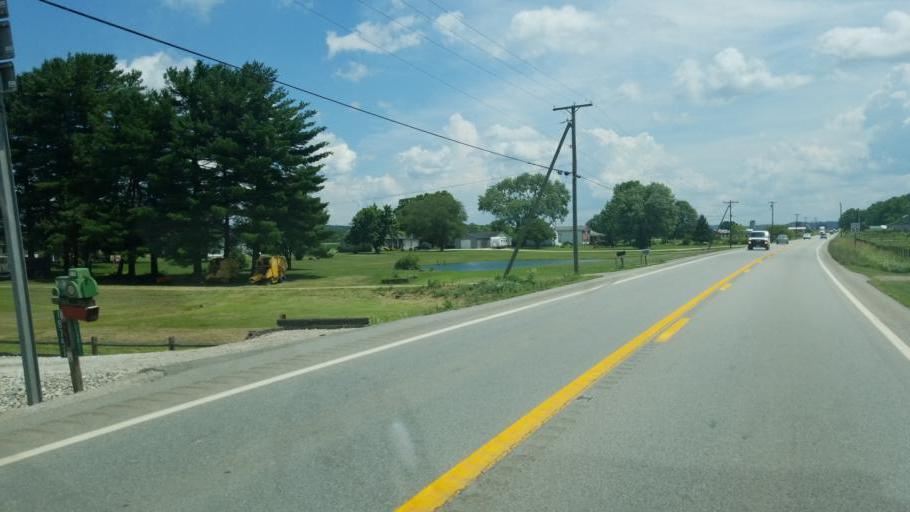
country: US
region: West Virginia
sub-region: Putnam County
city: Buffalo
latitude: 38.7642
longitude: -82.0016
